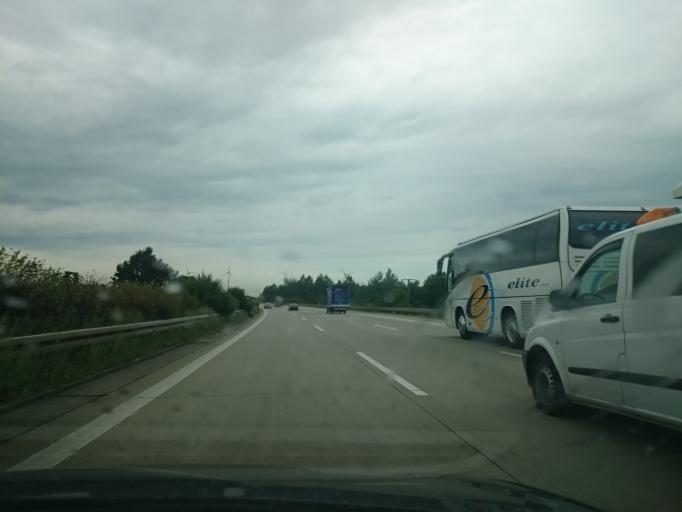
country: DE
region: Brandenburg
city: Borkheide
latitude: 52.1923
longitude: 12.8604
